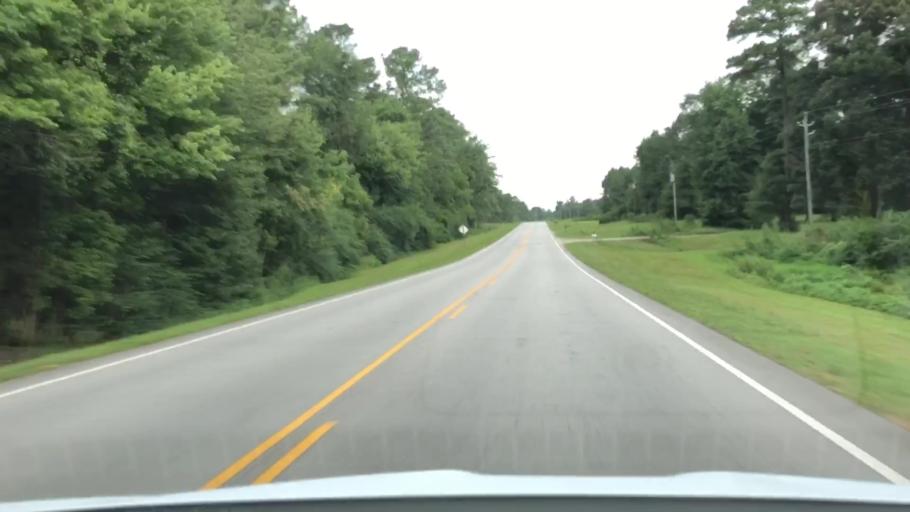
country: US
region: North Carolina
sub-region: Jones County
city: Trenton
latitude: 35.0122
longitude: -77.2909
